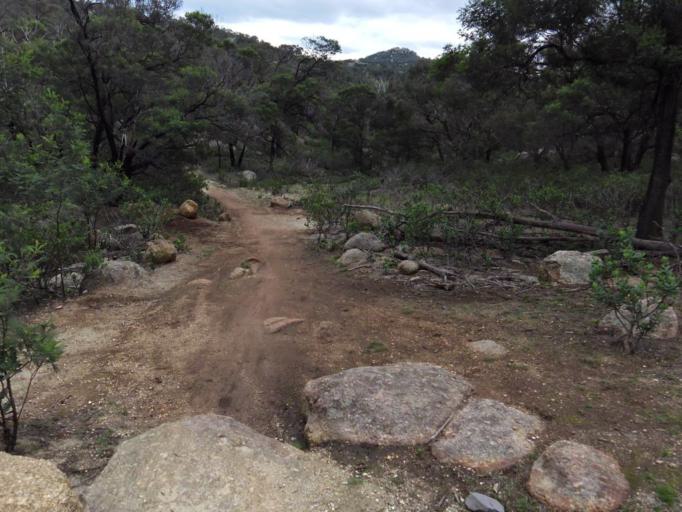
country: AU
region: Victoria
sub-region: Wyndham
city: Little River
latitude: -37.9334
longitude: 144.4376
